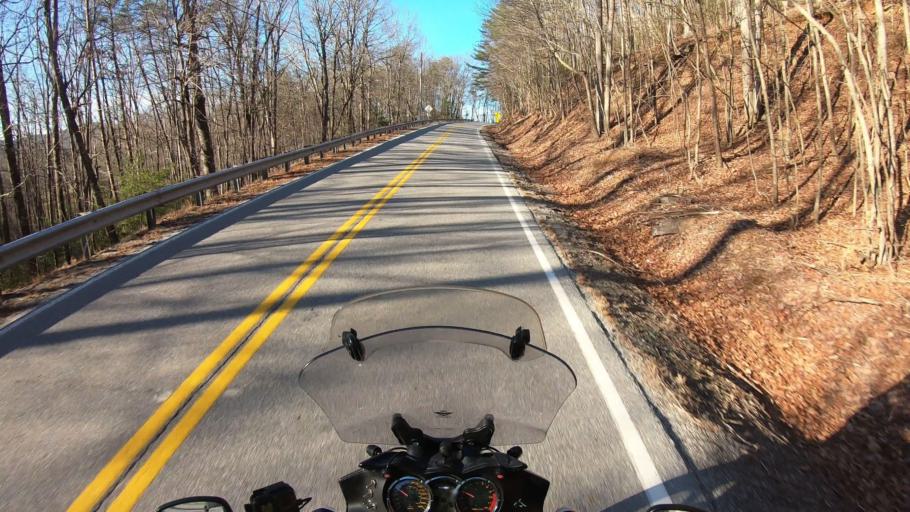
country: US
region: Georgia
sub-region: Lumpkin County
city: Dahlonega
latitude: 34.6867
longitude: -84.0115
